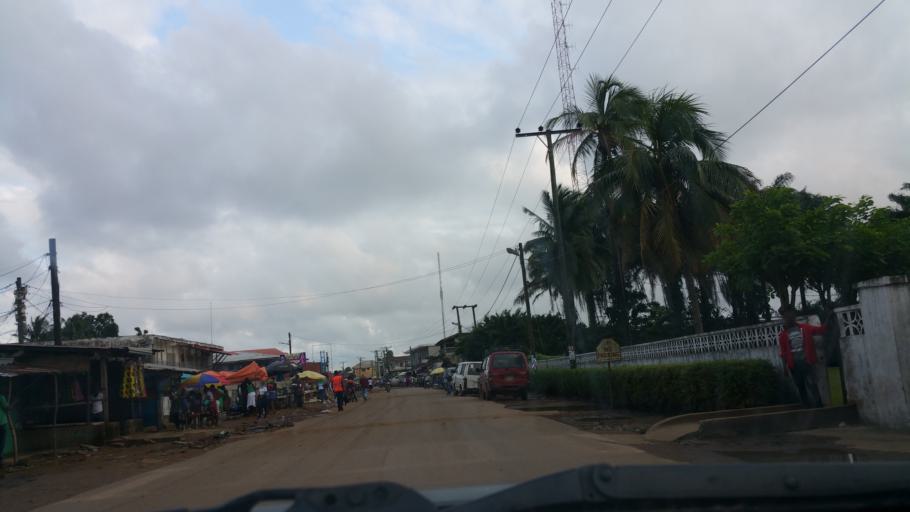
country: LR
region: Montserrado
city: Monrovia
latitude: 6.2798
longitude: -10.7497
